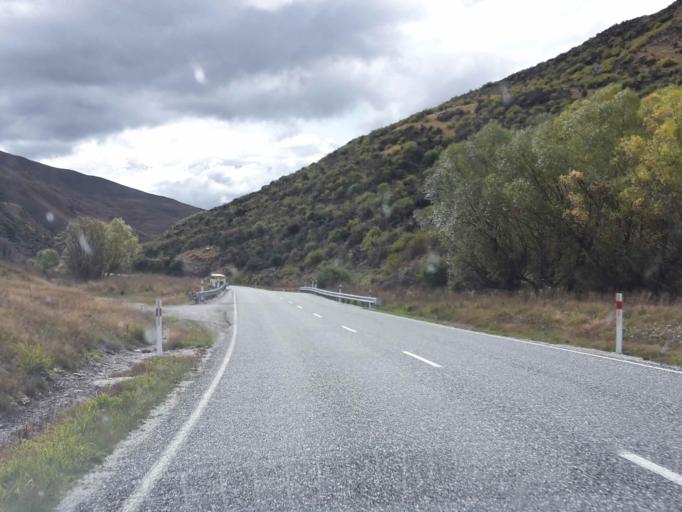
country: NZ
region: Otago
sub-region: Queenstown-Lakes District
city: Arrowtown
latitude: -44.9278
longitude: 168.9714
